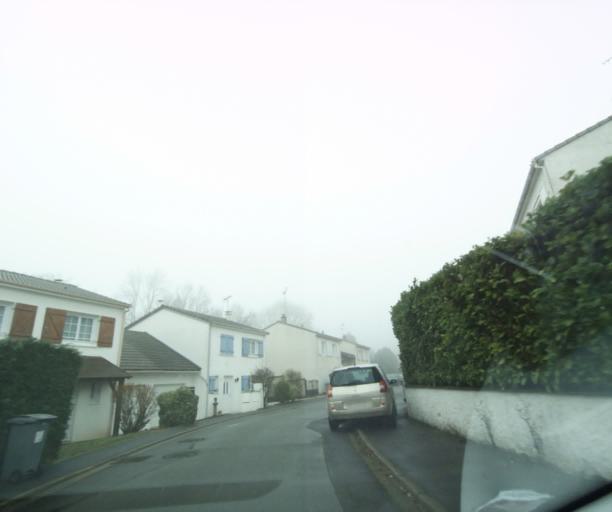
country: FR
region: Ile-de-France
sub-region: Departement de Seine-et-Marne
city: Dammartin-en-Goele
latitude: 49.0559
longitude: 2.6946
